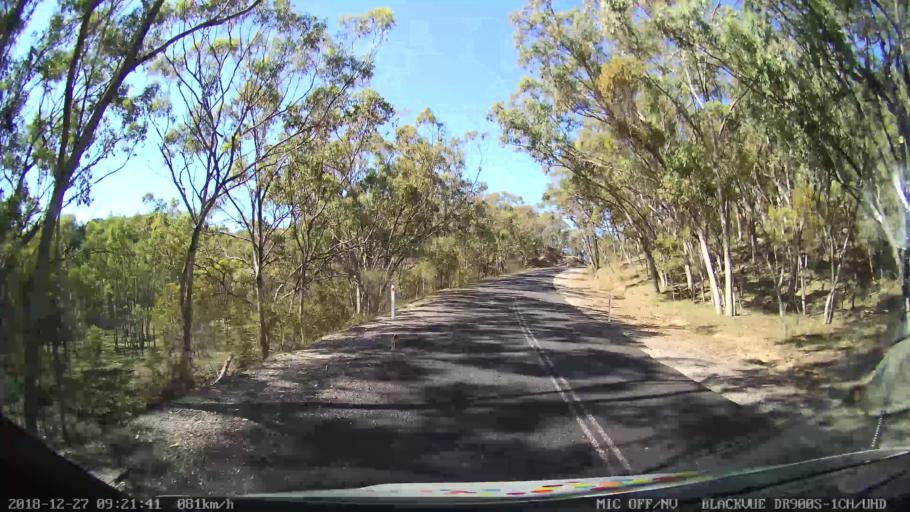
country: AU
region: New South Wales
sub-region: Lithgow
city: Portland
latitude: -33.1264
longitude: 150.0156
